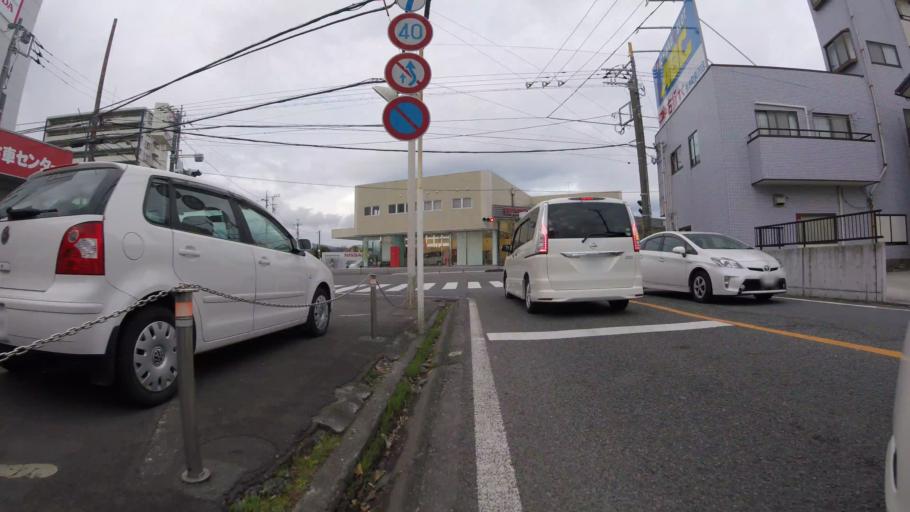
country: JP
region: Shizuoka
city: Numazu
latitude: 35.1085
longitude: 138.8914
